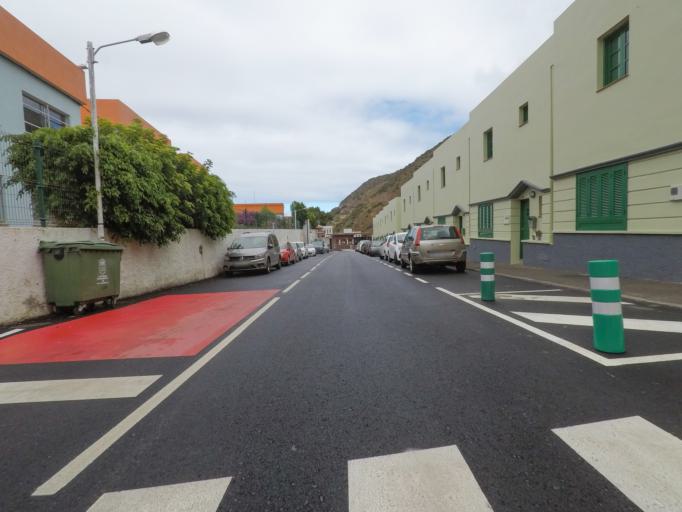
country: ES
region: Canary Islands
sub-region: Provincia de Santa Cruz de Tenerife
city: Vallehermosa
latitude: 28.1808
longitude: -17.2649
